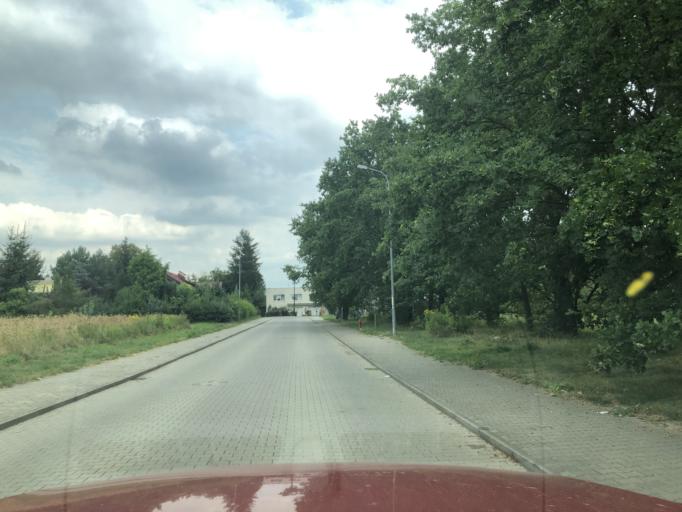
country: PL
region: Lower Silesian Voivodeship
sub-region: Powiat wroclawski
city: Smolec
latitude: 51.1572
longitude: 16.9047
